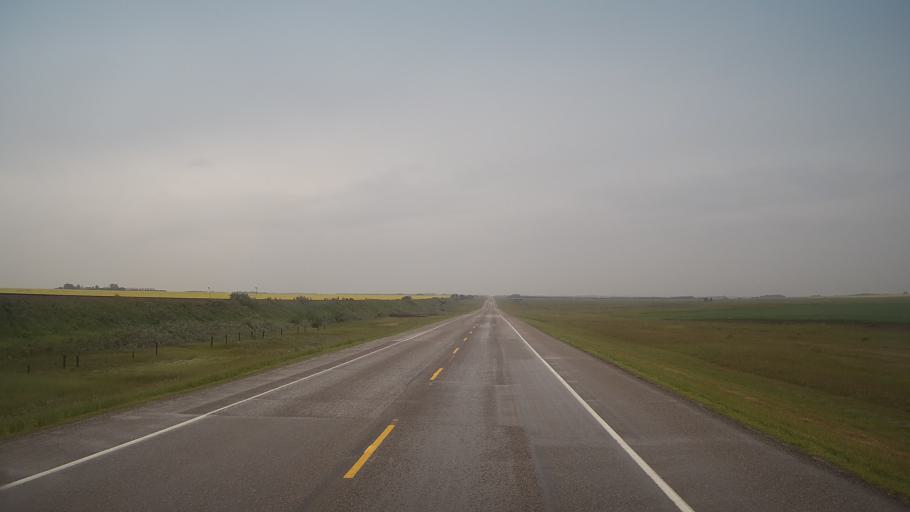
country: CA
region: Saskatchewan
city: Wilkie
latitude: 52.2129
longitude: -108.4964
